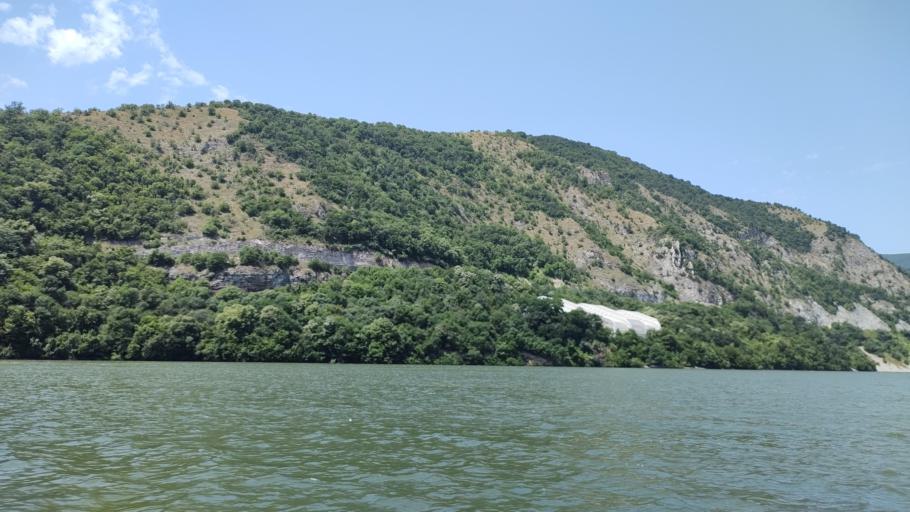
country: RO
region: Mehedinti
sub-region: Comuna Svinita
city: Svinita
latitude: 44.5547
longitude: 22.0310
